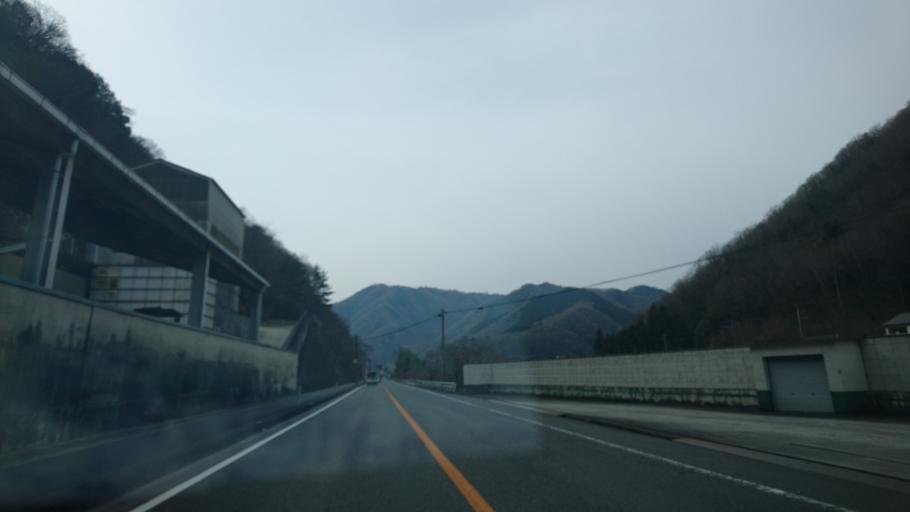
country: JP
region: Okayama
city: Takahashi
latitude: 34.8270
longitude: 133.6234
